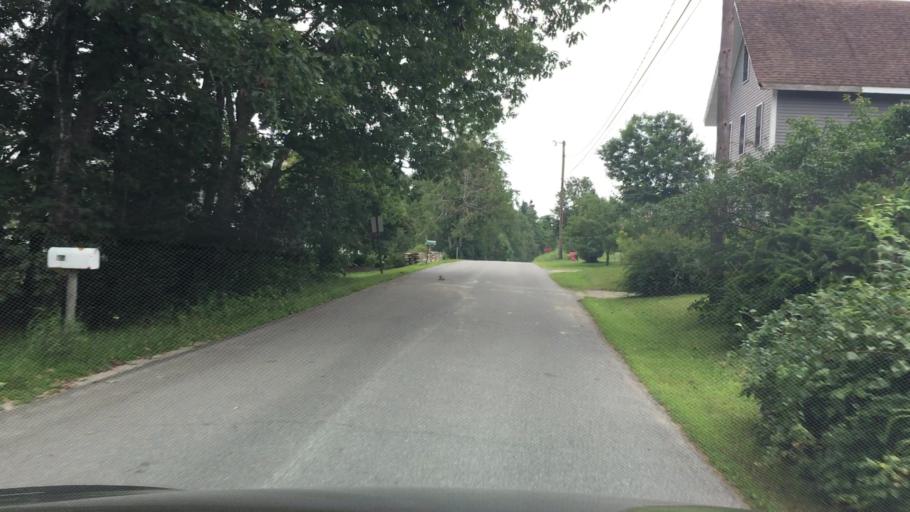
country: US
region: Maine
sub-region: Waldo County
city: Stockton Springs
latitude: 44.5078
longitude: -68.8102
